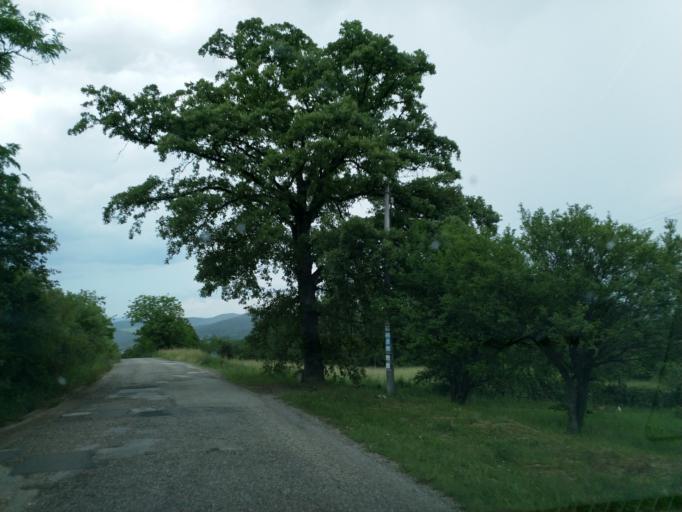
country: RS
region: Central Serbia
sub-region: Borski Okrug
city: Bor
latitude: 43.9924
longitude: 21.9774
